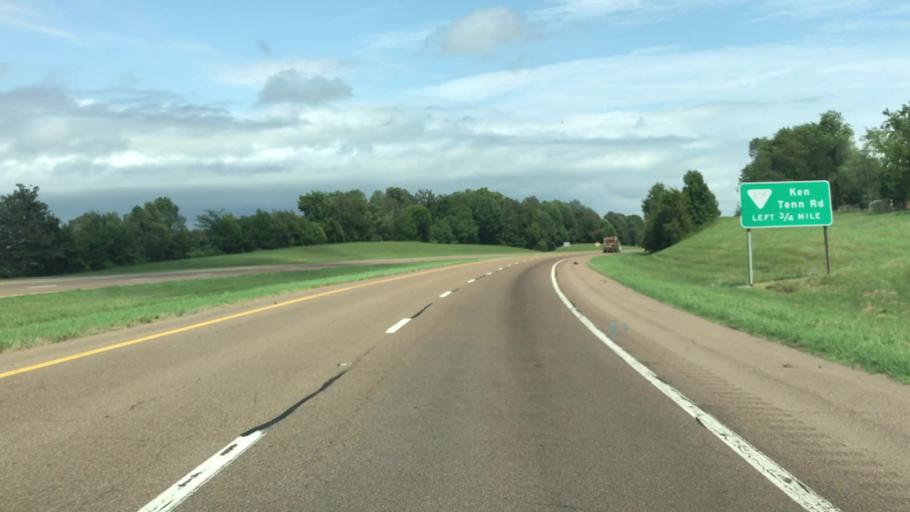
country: US
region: Tennessee
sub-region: Obion County
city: South Fulton
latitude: 36.4941
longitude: -88.9150
